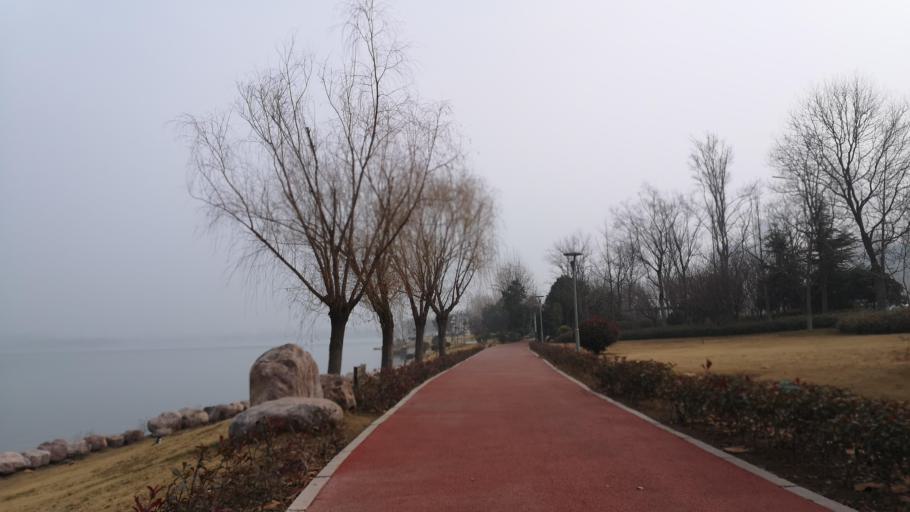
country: CN
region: Henan Sheng
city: Zhongyuanlu
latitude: 35.8004
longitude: 115.0474
